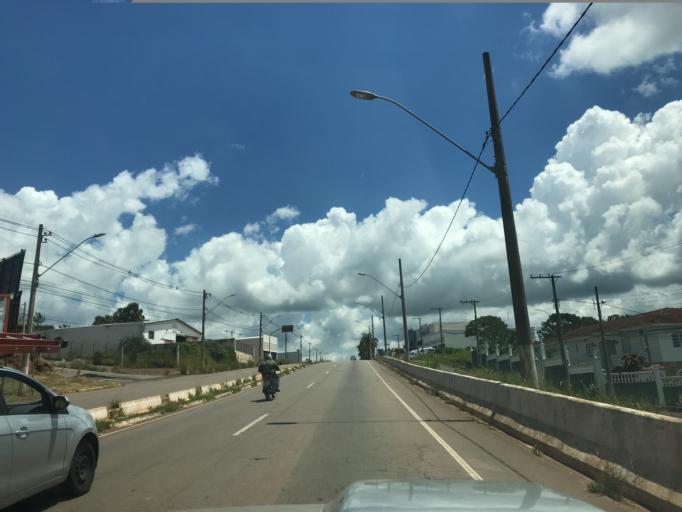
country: BR
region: Minas Gerais
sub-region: Tres Coracoes
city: Tres Coracoes
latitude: -21.6718
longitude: -45.2725
